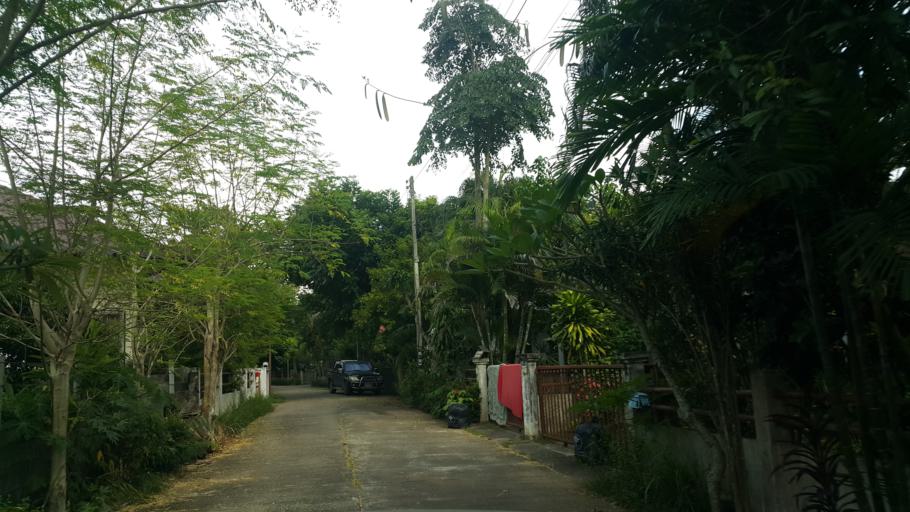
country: TH
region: Chiang Mai
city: San Sai
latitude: 18.8621
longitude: 99.0958
